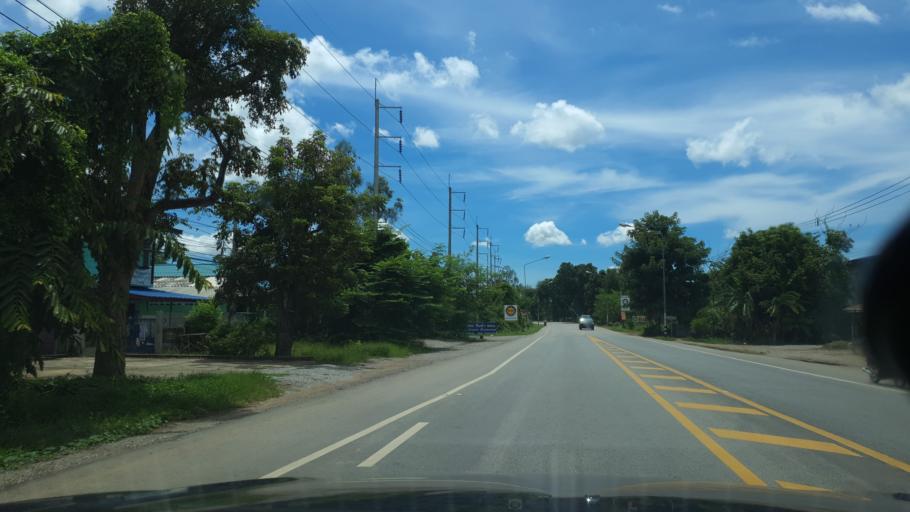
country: TH
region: Sukhothai
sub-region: Amphoe Si Satchanalai
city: Si Satchanalai
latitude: 17.5075
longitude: 99.7581
